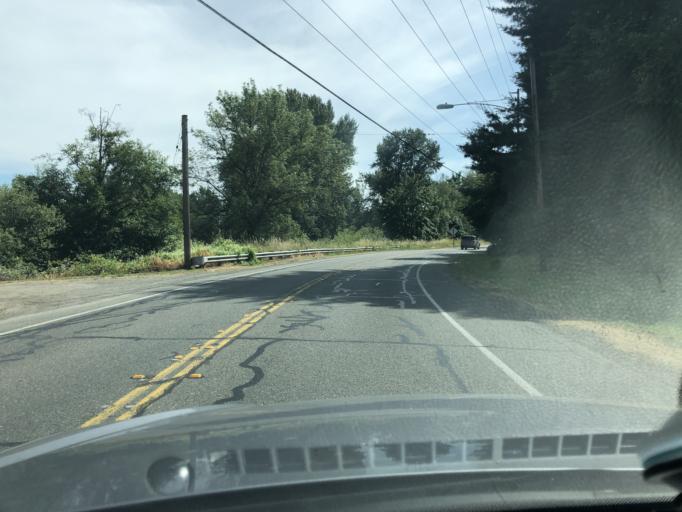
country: US
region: Washington
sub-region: King County
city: Kent
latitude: 47.3729
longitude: -122.2473
